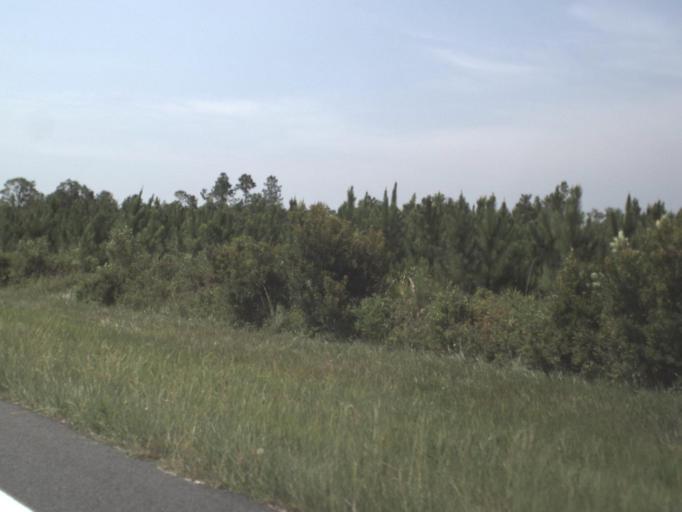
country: US
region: Georgia
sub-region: Echols County
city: Statenville
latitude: 30.6109
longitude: -83.0217
